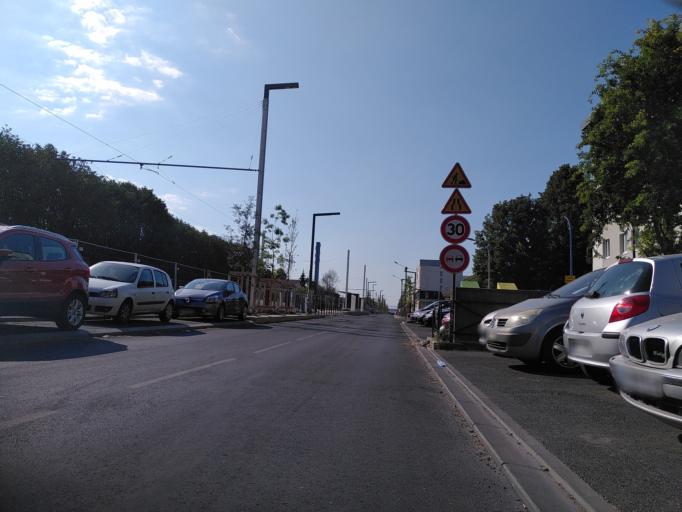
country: FR
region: Ile-de-France
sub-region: Departement du Val-de-Marne
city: Choisy-le-Roi
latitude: 48.7529
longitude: 2.4163
